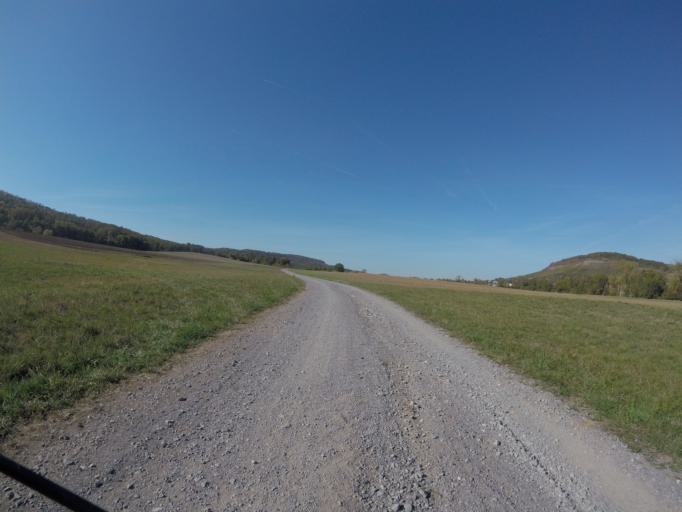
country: DE
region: Baden-Wuerttemberg
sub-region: Karlsruhe Region
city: Illingen
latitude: 48.9902
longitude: 8.9207
